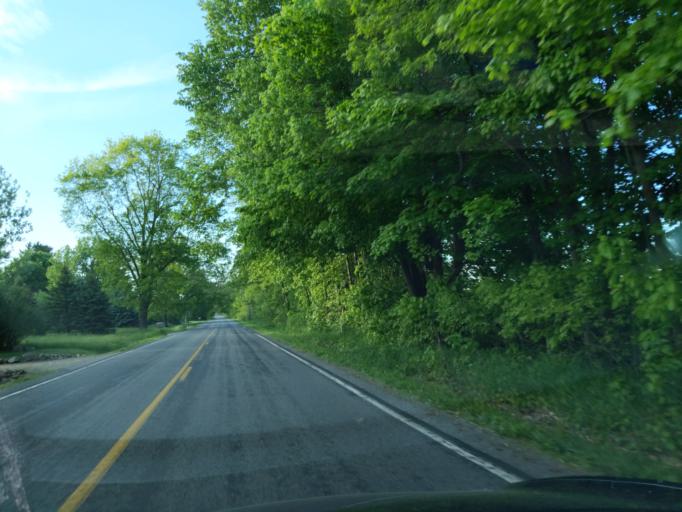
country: US
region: Michigan
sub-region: Ingham County
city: Leslie
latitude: 42.4496
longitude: -84.3132
